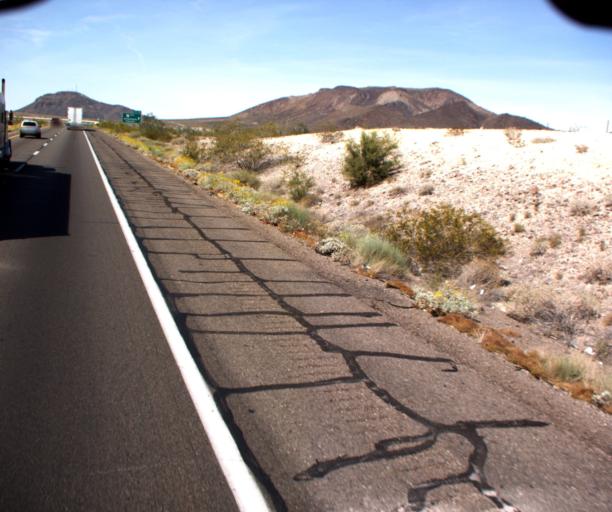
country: US
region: Arizona
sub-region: La Paz County
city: Quartzsite
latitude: 33.6610
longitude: -114.0026
